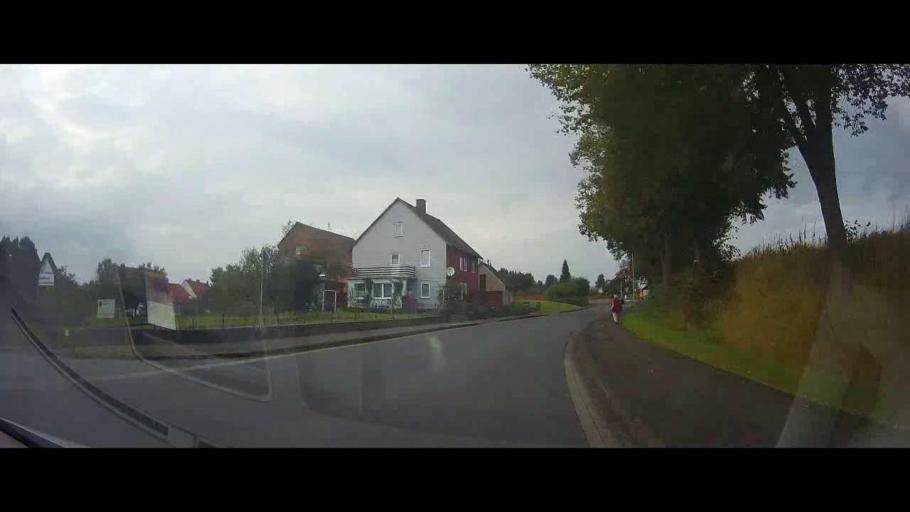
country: DE
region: Lower Saxony
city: Uslar
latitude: 51.6081
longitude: 9.6736
